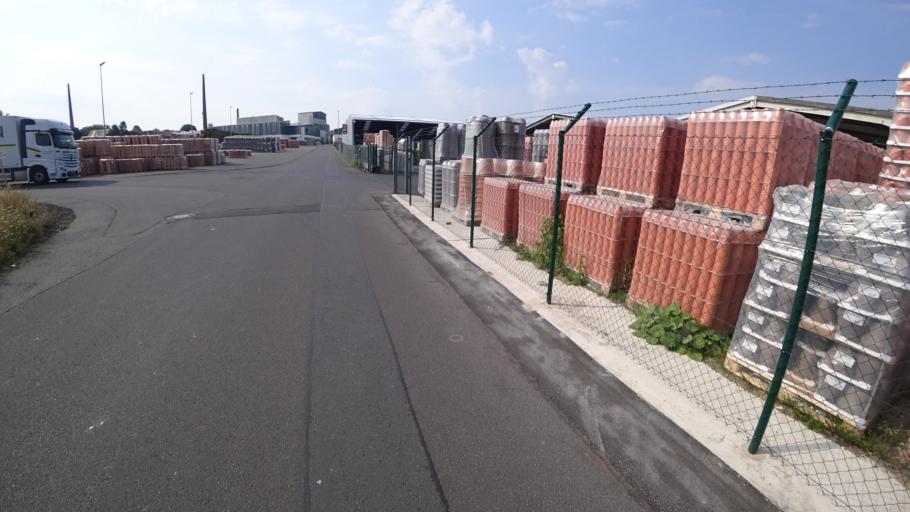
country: DE
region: Rheinland-Pfalz
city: Hundsdorf
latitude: 50.4623
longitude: 7.7206
